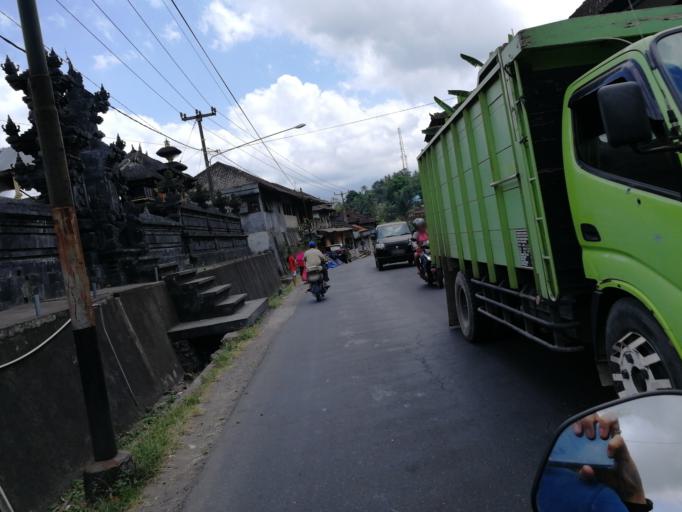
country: ID
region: Bali
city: Banjar Wangsian
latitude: -8.4636
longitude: 115.4482
